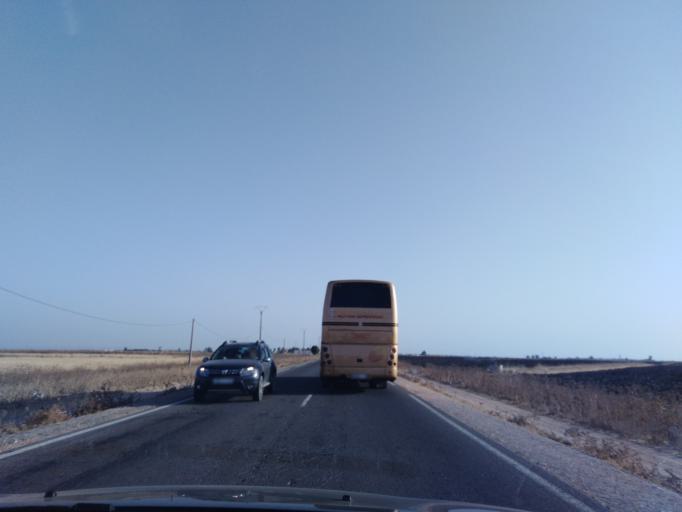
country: MA
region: Doukkala-Abda
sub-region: Safi
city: Youssoufia
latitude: 32.4832
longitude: -8.7684
